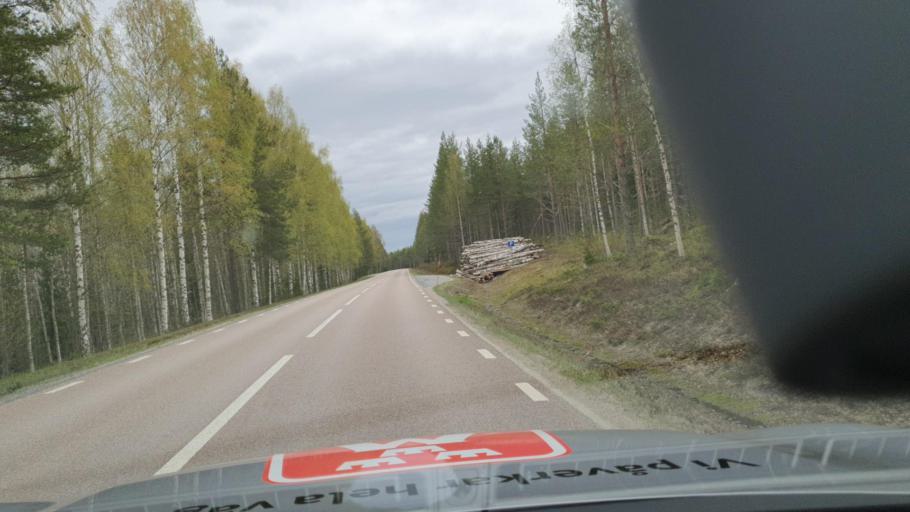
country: SE
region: Vaesternorrland
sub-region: OErnskoeldsviks Kommun
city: Ornskoldsvik
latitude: 63.4937
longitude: 18.8717
